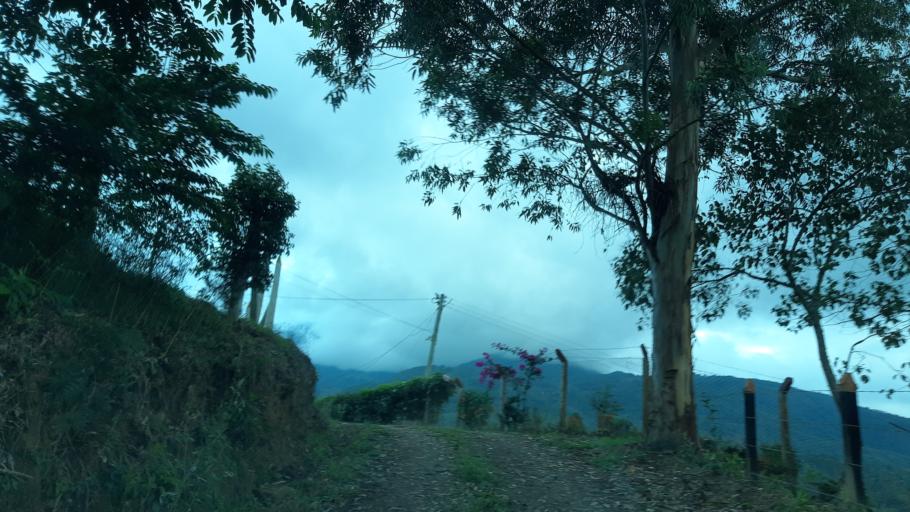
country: CO
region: Boyaca
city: Chinavita
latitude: 5.1343
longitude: -73.3499
